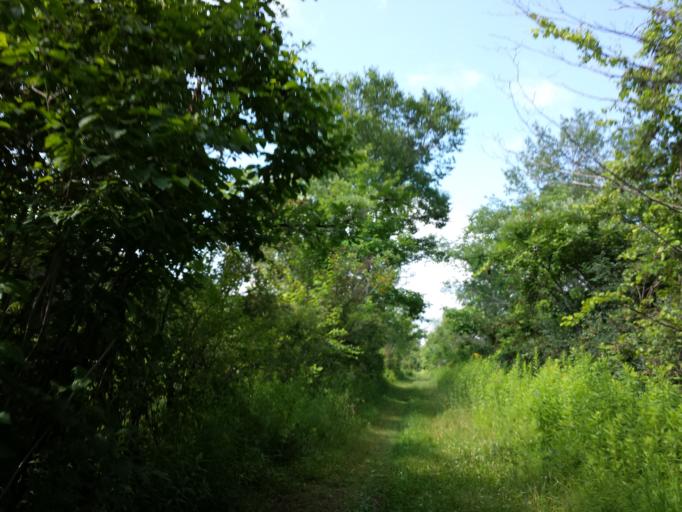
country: US
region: Vermont
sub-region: Rutland County
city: Poultney
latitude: 43.4999
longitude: -73.2417
